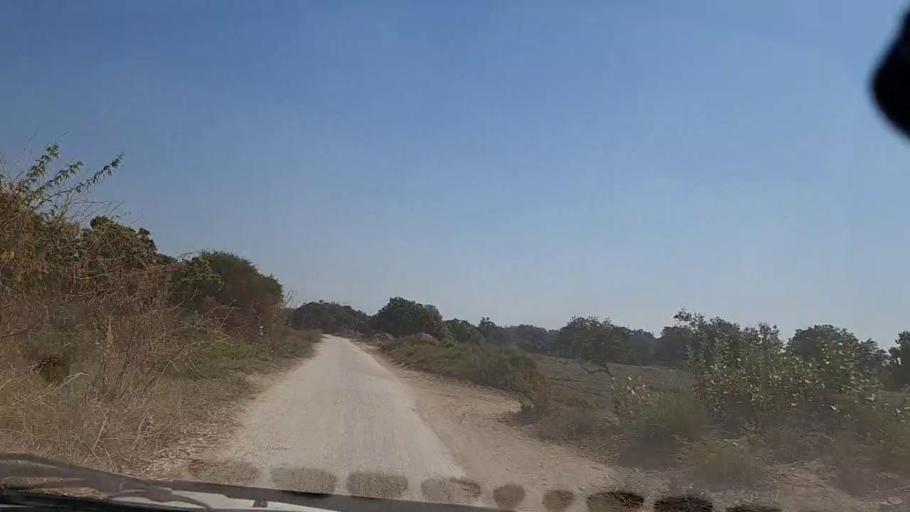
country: PK
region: Sindh
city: Mirpur Khas
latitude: 25.4708
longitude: 69.0345
